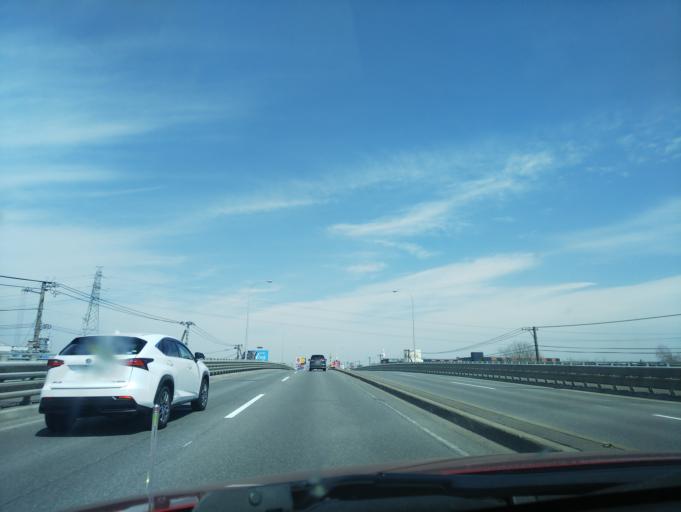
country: JP
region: Hokkaido
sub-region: Asahikawa-shi
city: Asahikawa
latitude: 43.7852
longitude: 142.3933
